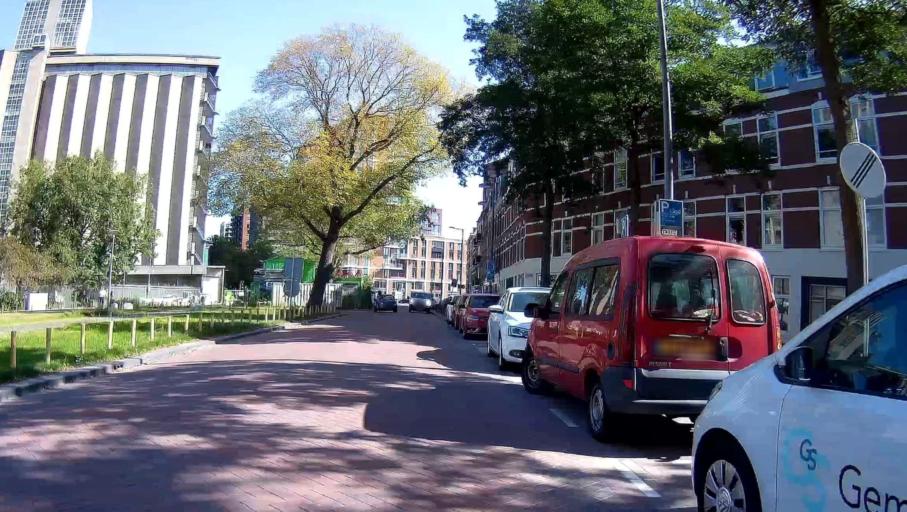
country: NL
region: South Holland
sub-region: Gemeente Rotterdam
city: Rotterdam
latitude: 51.9016
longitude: 4.4886
